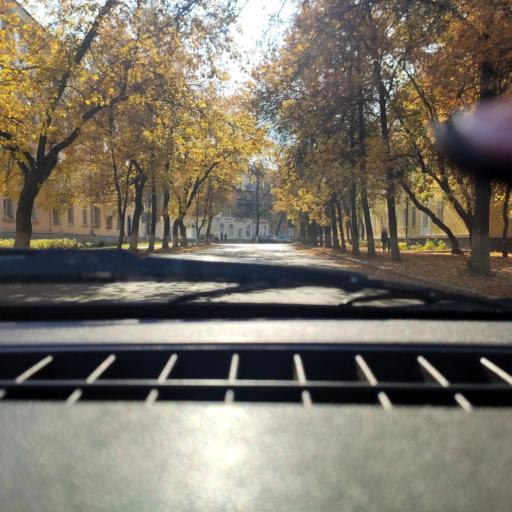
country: RU
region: Bashkortostan
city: Ufa
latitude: 54.8211
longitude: 56.0710
